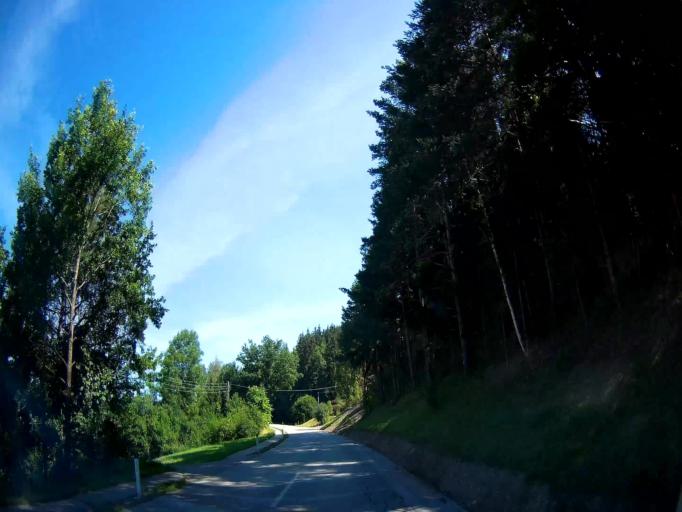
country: AT
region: Carinthia
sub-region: Politischer Bezirk Sankt Veit an der Glan
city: St. Georgen am Laengsee
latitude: 46.7692
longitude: 14.4229
